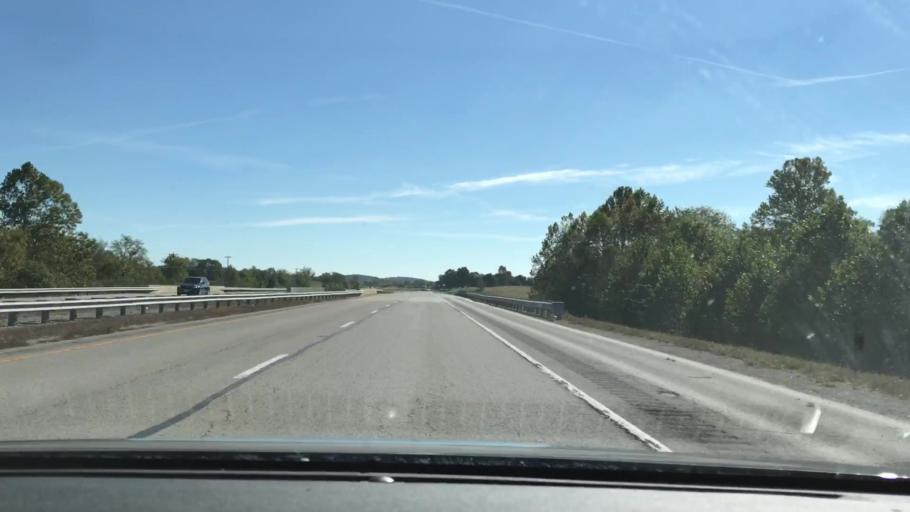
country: US
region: Kentucky
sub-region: Todd County
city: Elkton
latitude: 36.8446
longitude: -87.2736
